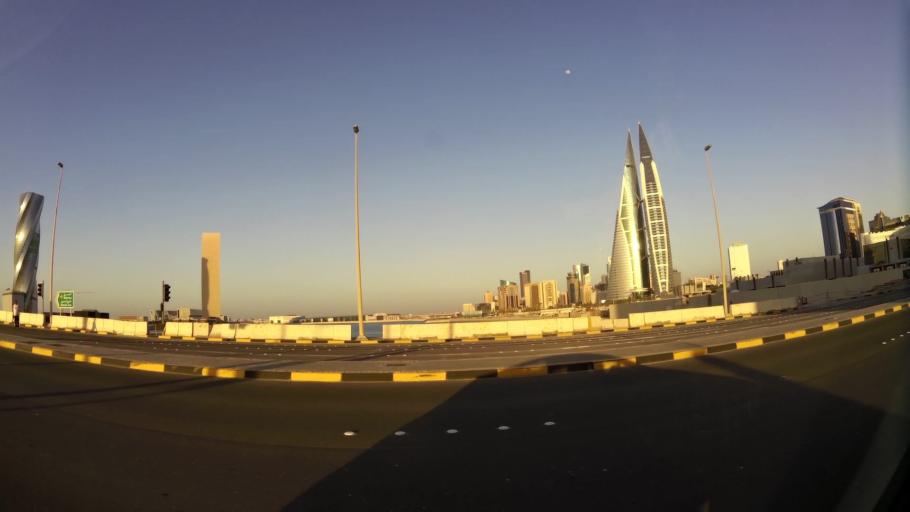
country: BH
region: Manama
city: Manama
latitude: 26.2398
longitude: 50.5756
